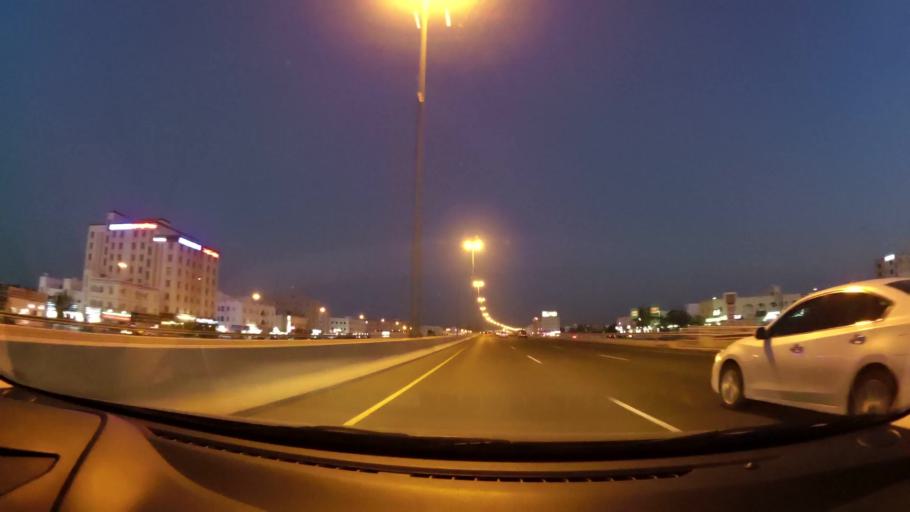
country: OM
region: Muhafazat Masqat
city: As Sib al Jadidah
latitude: 23.6303
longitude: 58.2330
